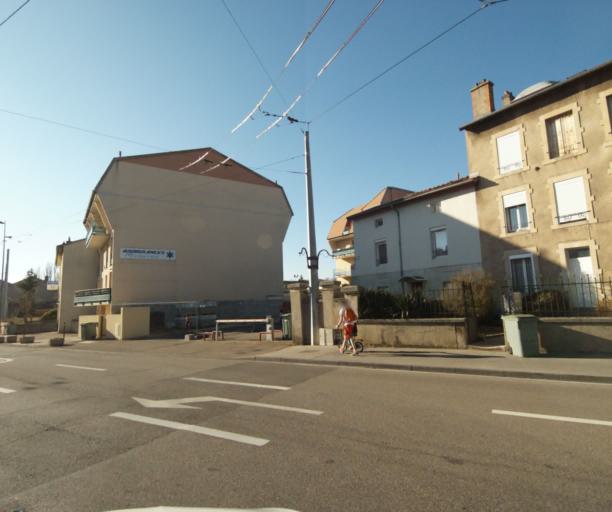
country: FR
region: Lorraine
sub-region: Departement de Meurthe-et-Moselle
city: Essey-les-Nancy
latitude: 48.7036
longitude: 6.2184
